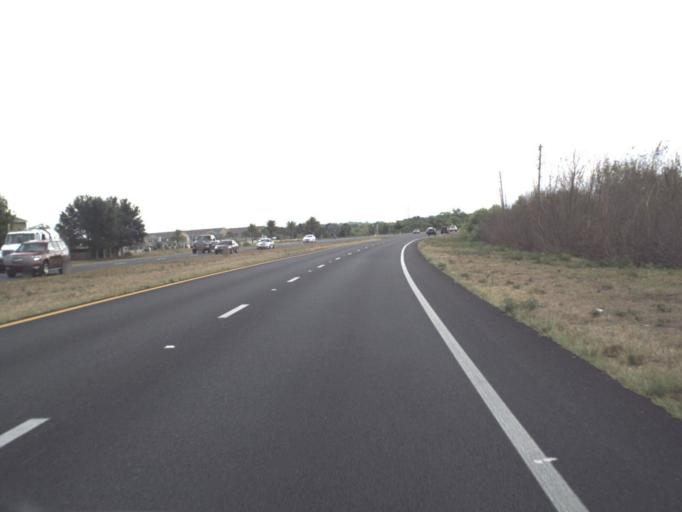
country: US
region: Florida
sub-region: Lake County
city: Clermont
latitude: 28.5581
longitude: -81.7914
